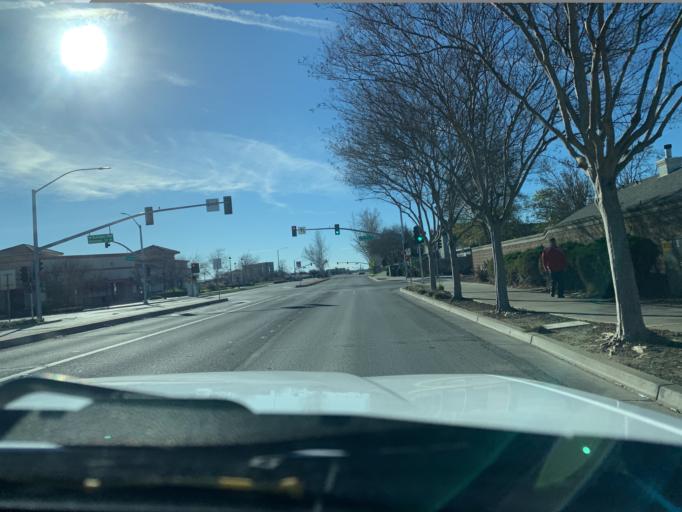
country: US
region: California
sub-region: Yolo County
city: Woodland
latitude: 38.6654
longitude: -121.7424
